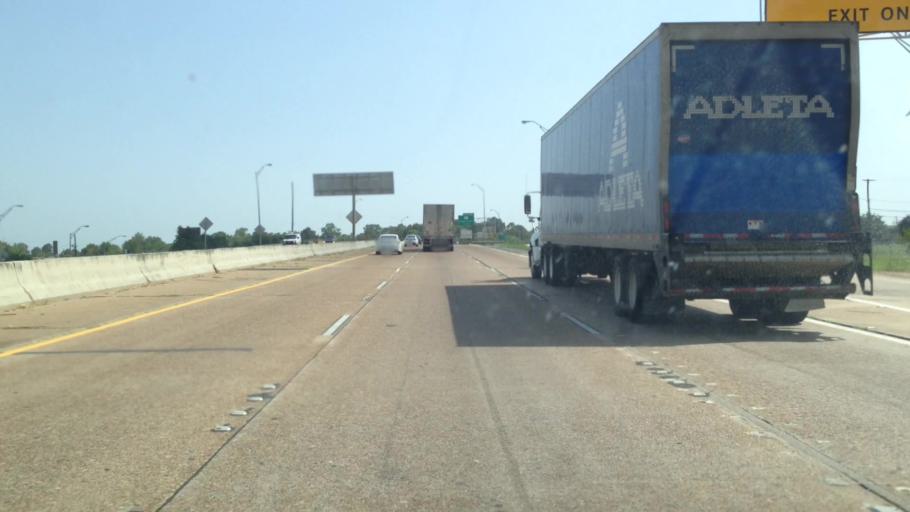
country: US
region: Louisiana
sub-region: Caddo Parish
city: Shreveport
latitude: 32.4875
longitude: -93.7734
